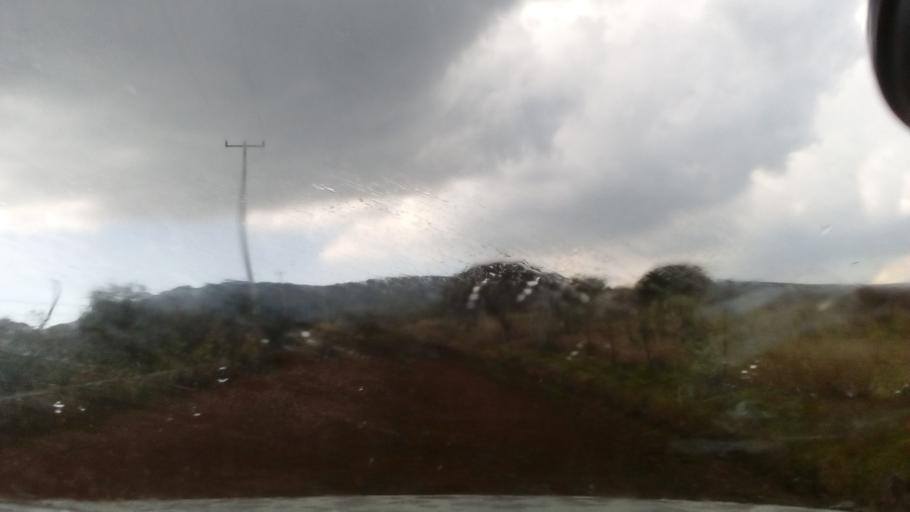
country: MX
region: Guanajuato
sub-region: Silao de la Victoria
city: San Francisco (Banos de Agua Caliente)
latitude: 21.1594
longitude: -101.4210
